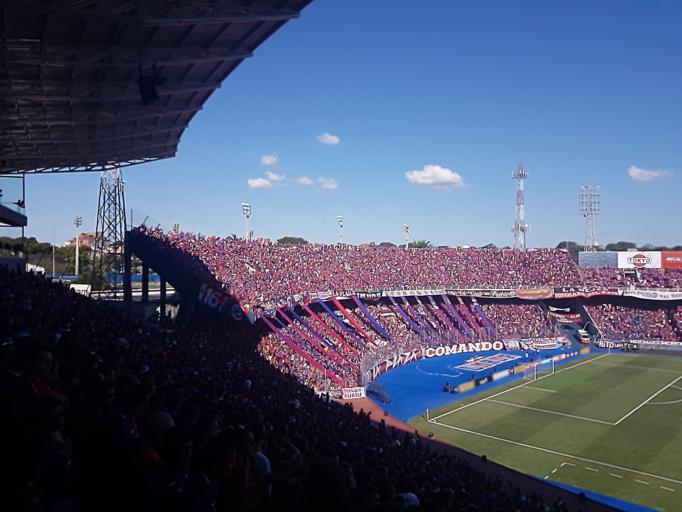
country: PY
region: Asuncion
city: Asuncion
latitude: -25.2995
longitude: -57.6369
